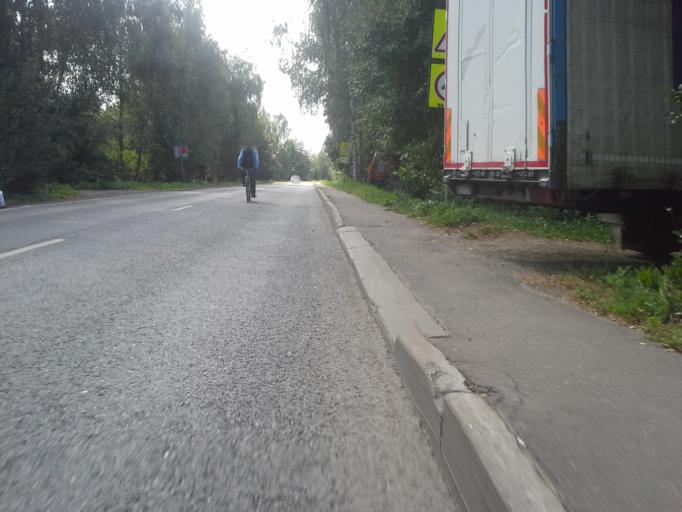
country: RU
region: Moskovskaya
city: Kokoshkino
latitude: 55.5767
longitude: 37.1306
